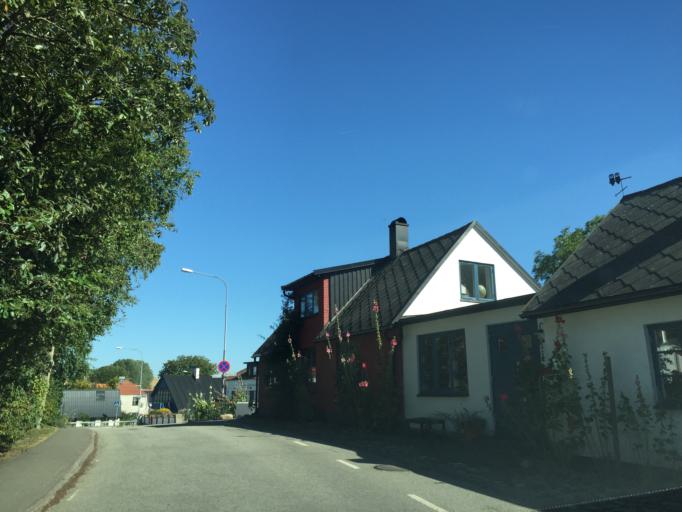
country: SE
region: Skane
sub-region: Ystads Kommun
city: Kopingebro
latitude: 55.3850
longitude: 14.0654
